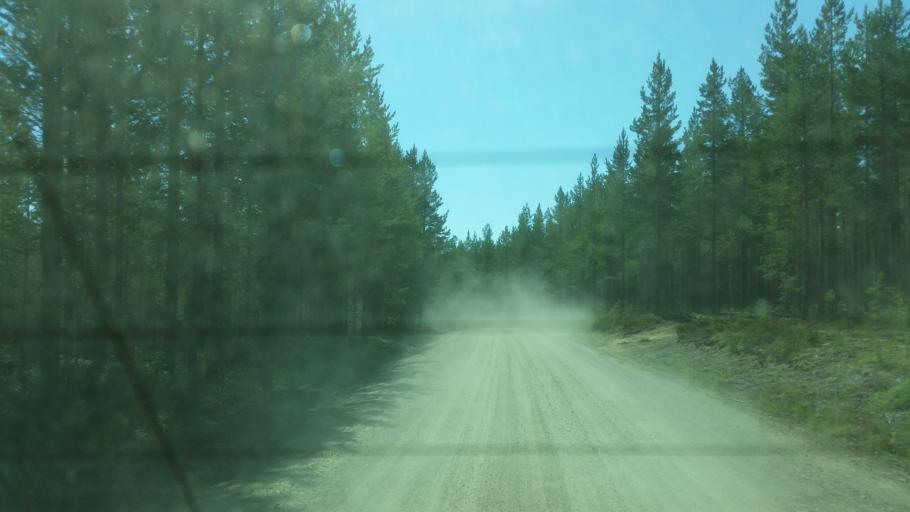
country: SE
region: Vaesternorrland
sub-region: Ange Kommun
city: Ange
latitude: 62.1915
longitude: 15.5906
